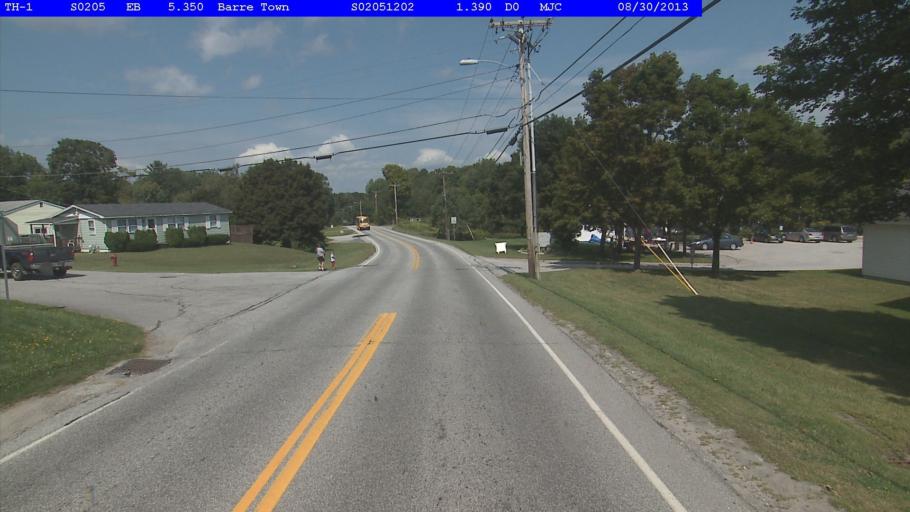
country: US
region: Vermont
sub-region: Washington County
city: South Barre
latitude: 44.1520
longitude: -72.4922
